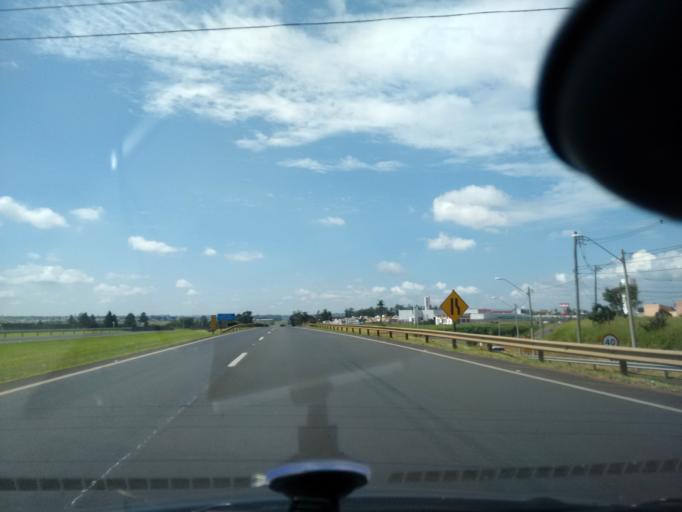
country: BR
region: Sao Paulo
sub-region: Sao Carlos
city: Sao Carlos
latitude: -21.9761
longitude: -47.9338
